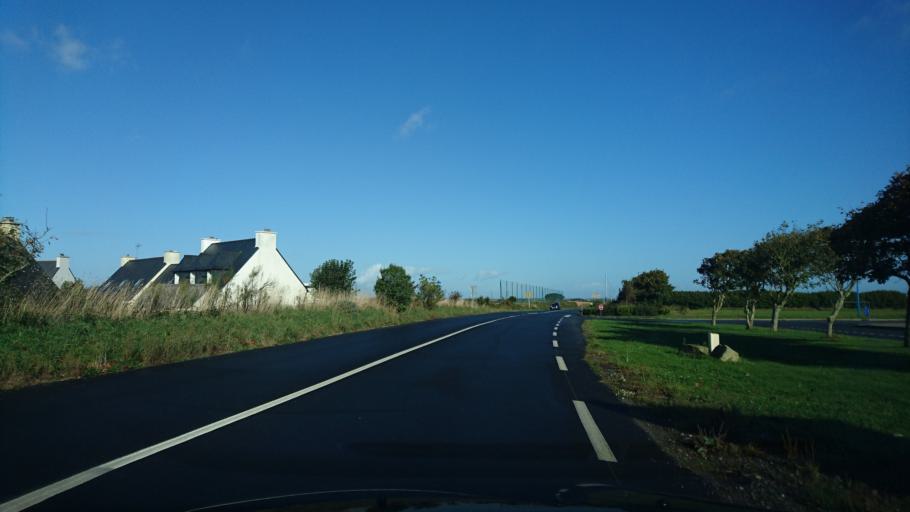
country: FR
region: Brittany
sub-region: Departement du Finistere
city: Plouarzel
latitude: 48.4342
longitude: -4.7150
